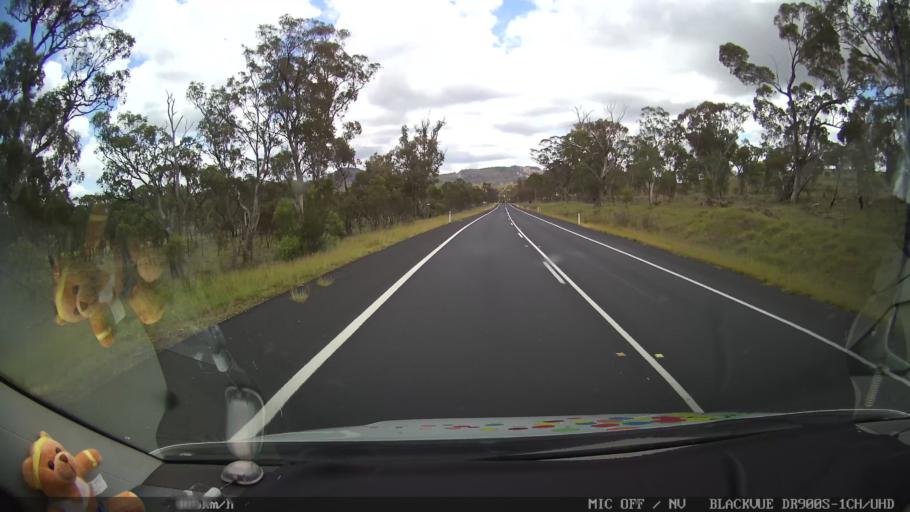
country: AU
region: New South Wales
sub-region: Glen Innes Severn
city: Glen Innes
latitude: -29.3719
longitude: 151.8936
